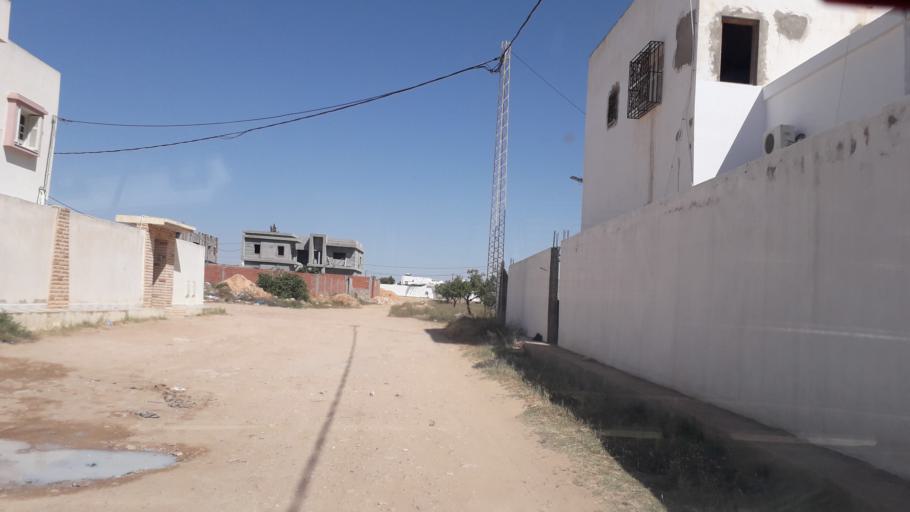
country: TN
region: Safaqis
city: Al Qarmadah
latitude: 34.8025
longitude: 10.7761
